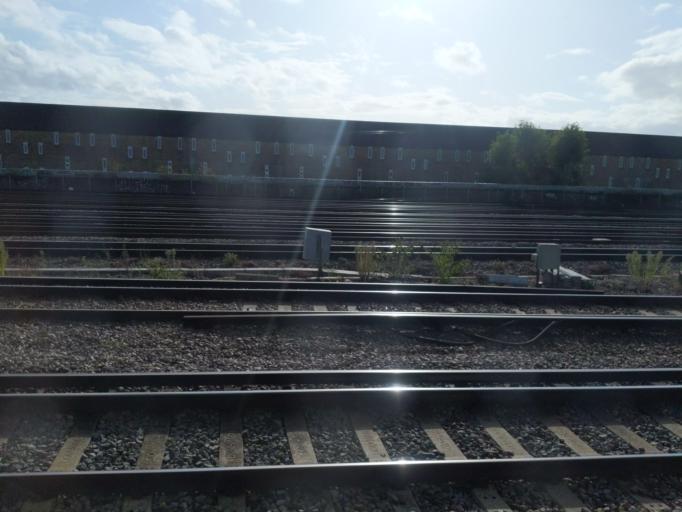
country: GB
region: England
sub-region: Greater London
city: City of London
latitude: 51.4950
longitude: -0.0659
